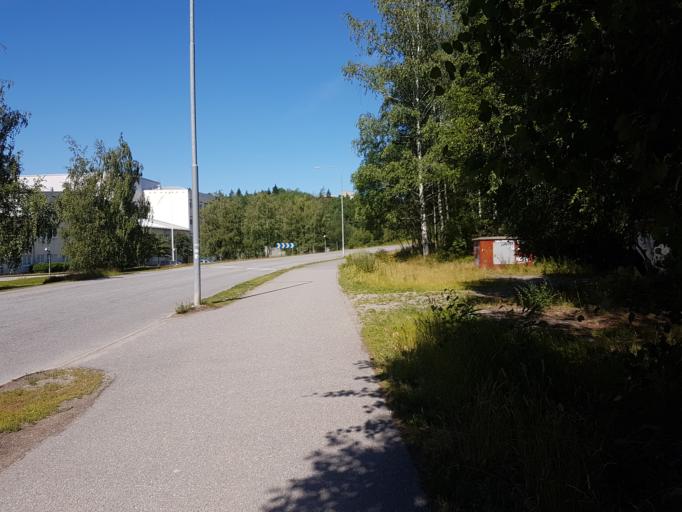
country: SE
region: Stockholm
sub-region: Huddinge Kommun
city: Huddinge
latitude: 59.2144
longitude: 17.9437
